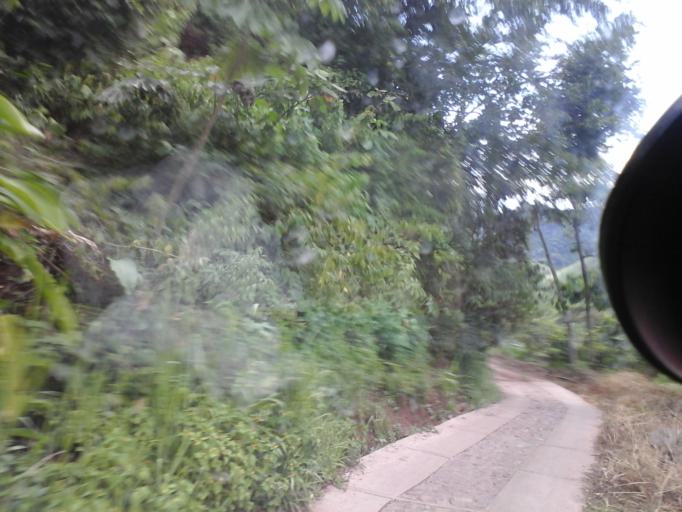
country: CO
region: Cesar
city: San Diego
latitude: 10.2710
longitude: -73.0879
